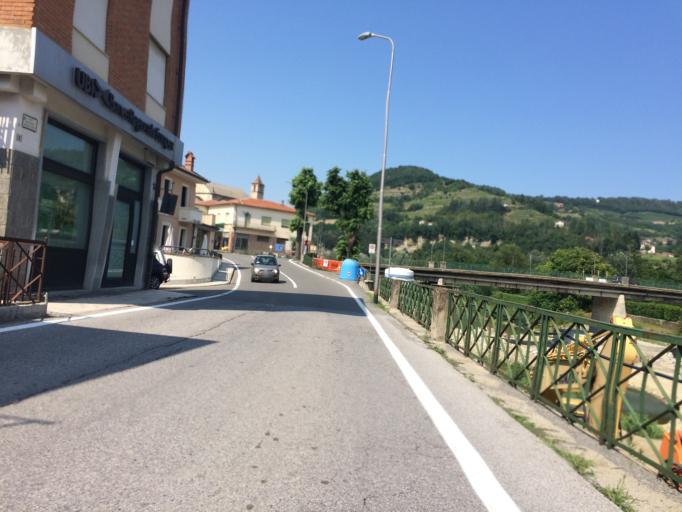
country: IT
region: Piedmont
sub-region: Provincia di Cuneo
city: Cortemilia
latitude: 44.5799
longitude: 8.1920
